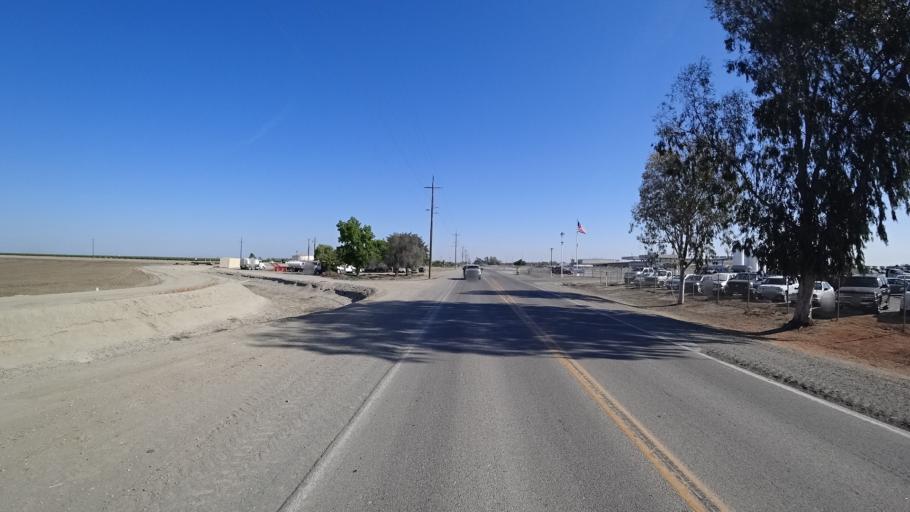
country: US
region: California
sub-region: Kings County
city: Corcoran
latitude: 36.0638
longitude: -119.5720
